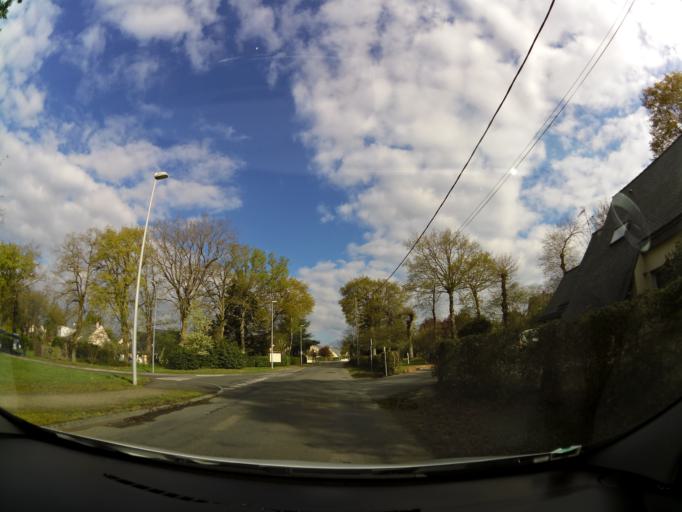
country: FR
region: Brittany
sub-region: Departement d'Ille-et-Vilaine
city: Laille
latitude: 47.9755
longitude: -1.7164
